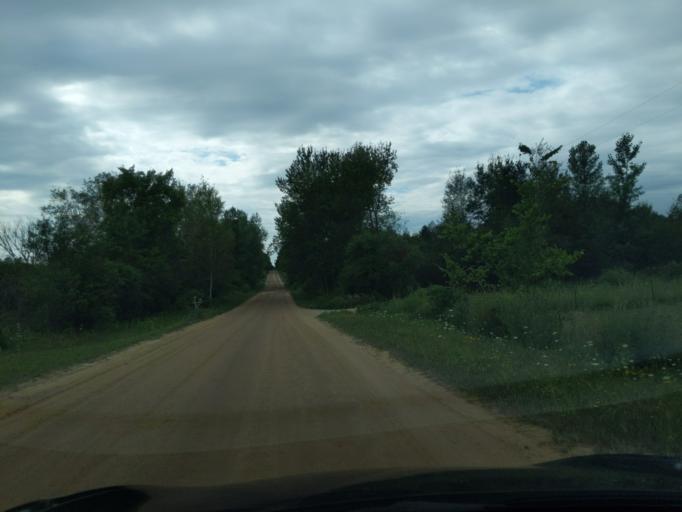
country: US
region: Michigan
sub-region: Clare County
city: Harrison
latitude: 44.0023
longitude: -85.0006
